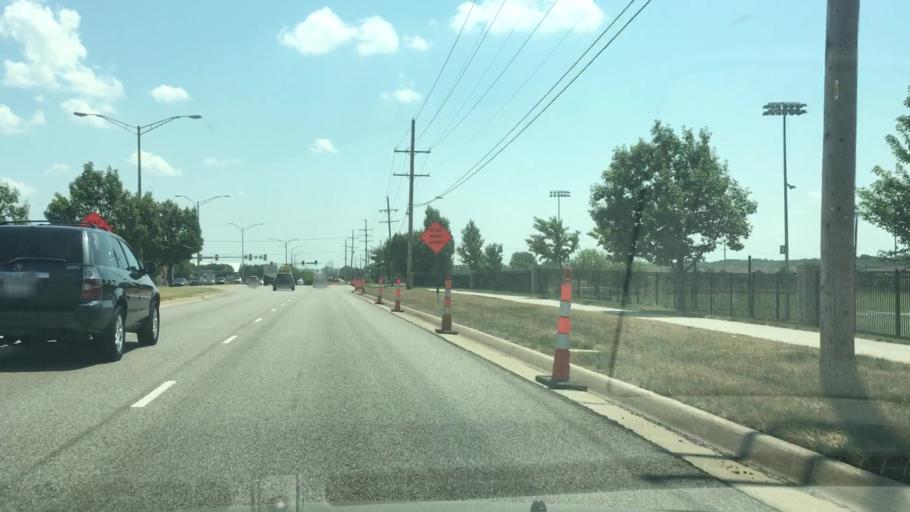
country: US
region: Kansas
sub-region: Johnson County
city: Lenexa
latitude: 38.8836
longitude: -94.7029
